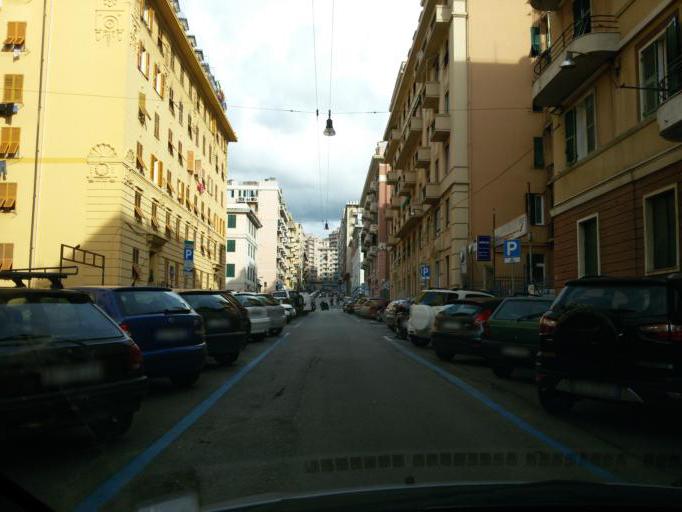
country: IT
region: Liguria
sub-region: Provincia di Genova
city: Genoa
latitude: 44.4103
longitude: 8.9559
